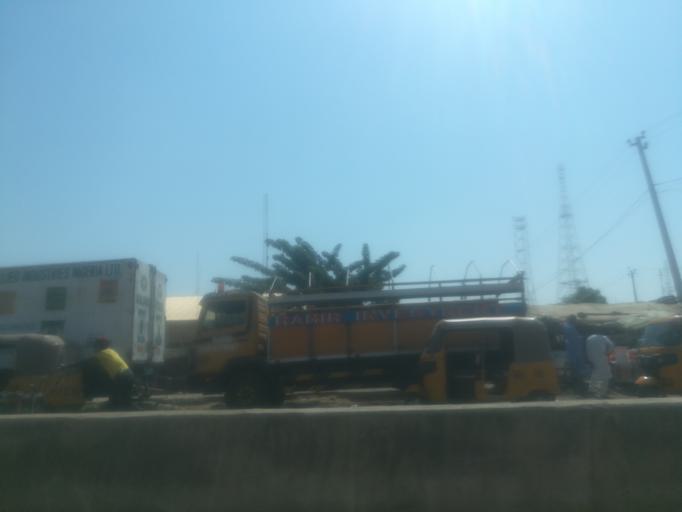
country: NG
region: Kano
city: Kano
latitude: 12.0053
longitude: 8.5376
